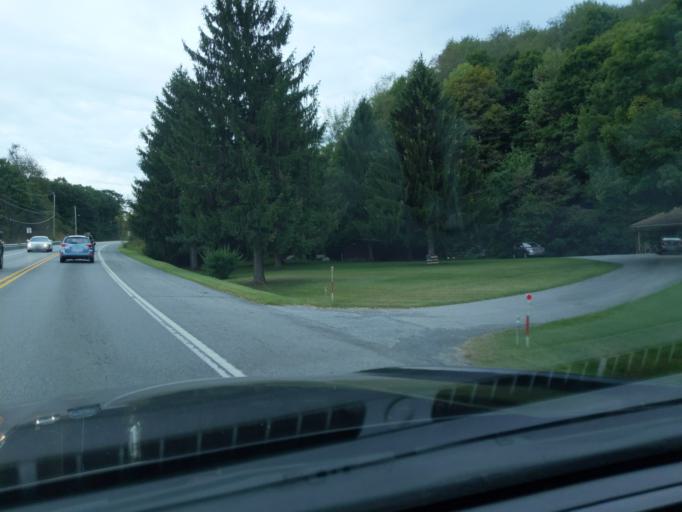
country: US
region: Pennsylvania
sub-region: Blair County
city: Duncansville
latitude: 40.3870
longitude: -78.4342
